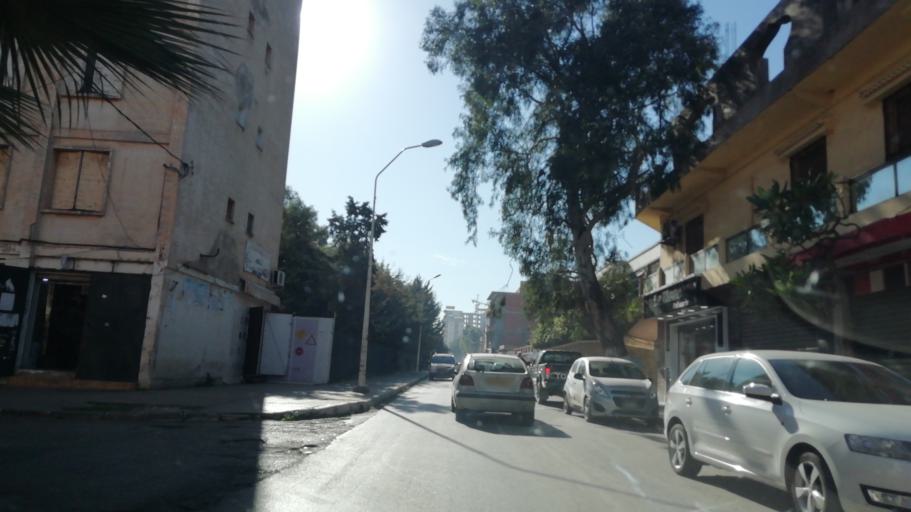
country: DZ
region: Oran
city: Oran
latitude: 35.6707
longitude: -0.6504
